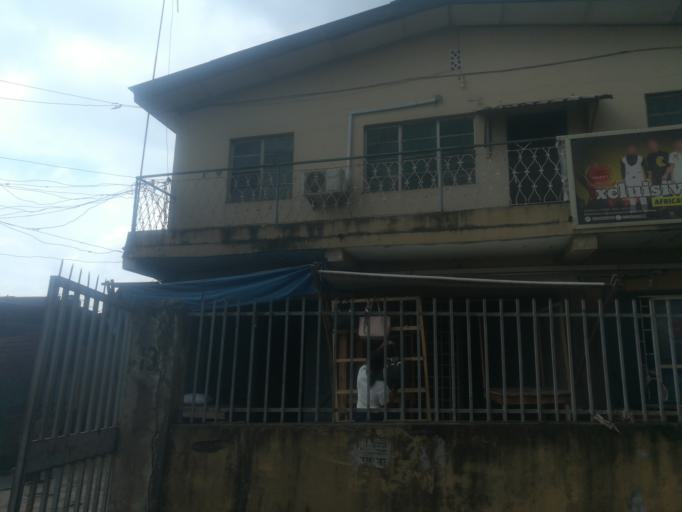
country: NG
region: Lagos
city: Ojota
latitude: 6.5932
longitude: 3.3863
